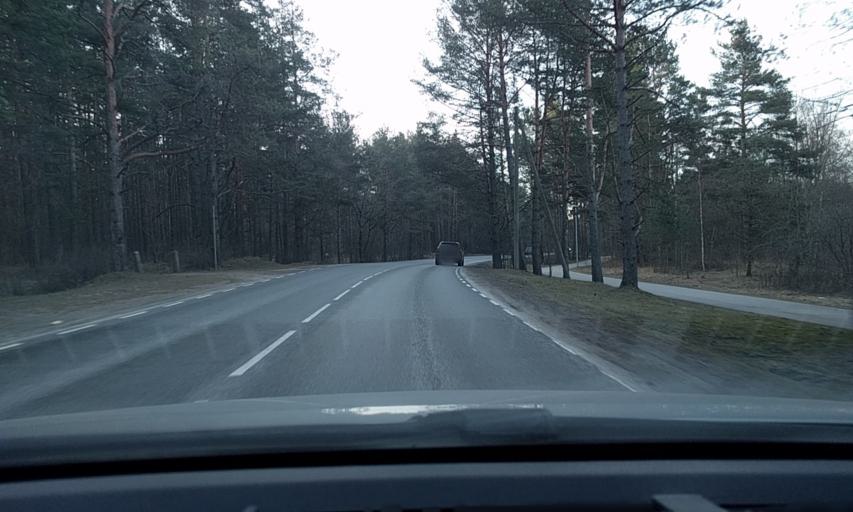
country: EE
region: Harju
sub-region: Tallinna linn
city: Kose
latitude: 59.4791
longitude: 24.8927
